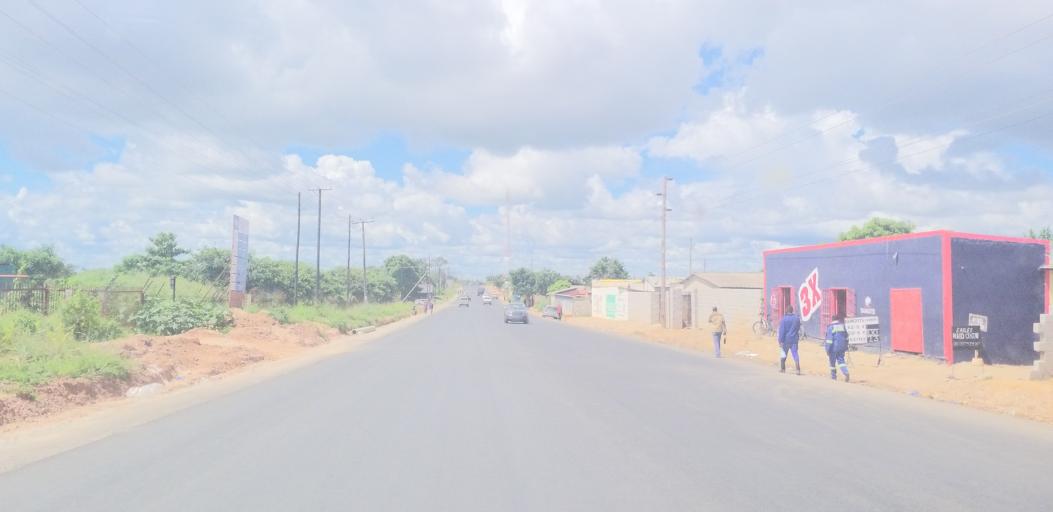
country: ZM
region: Lusaka
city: Lusaka
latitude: -15.3635
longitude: 28.3211
